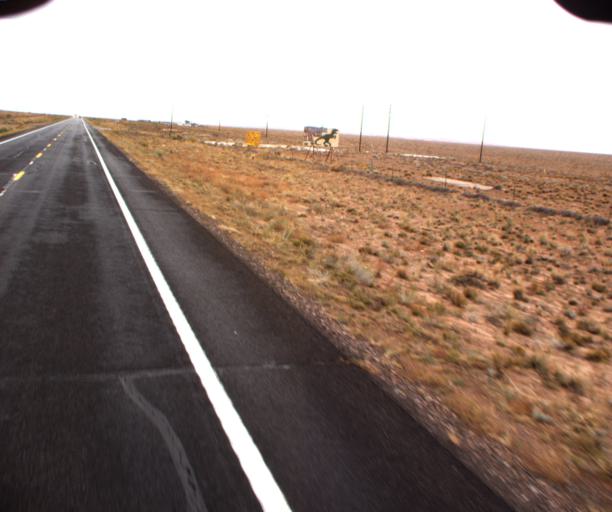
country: US
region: Arizona
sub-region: Coconino County
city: Tuba City
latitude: 36.1502
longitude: -111.1349
